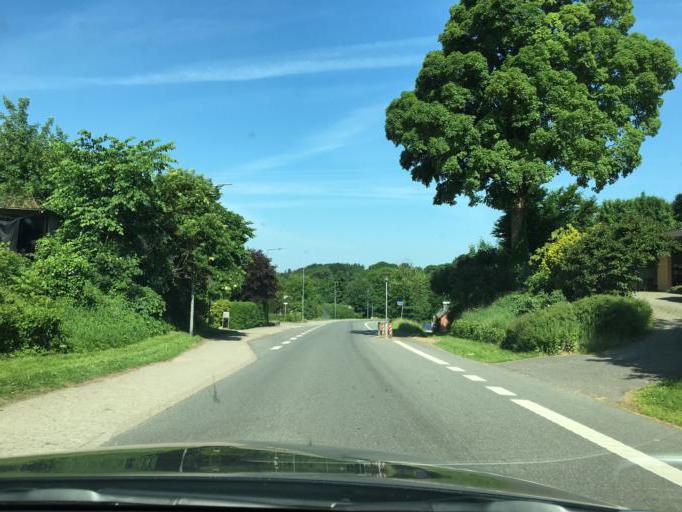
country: DK
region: South Denmark
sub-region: Kolding Kommune
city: Kolding
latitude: 55.5665
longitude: 9.4899
